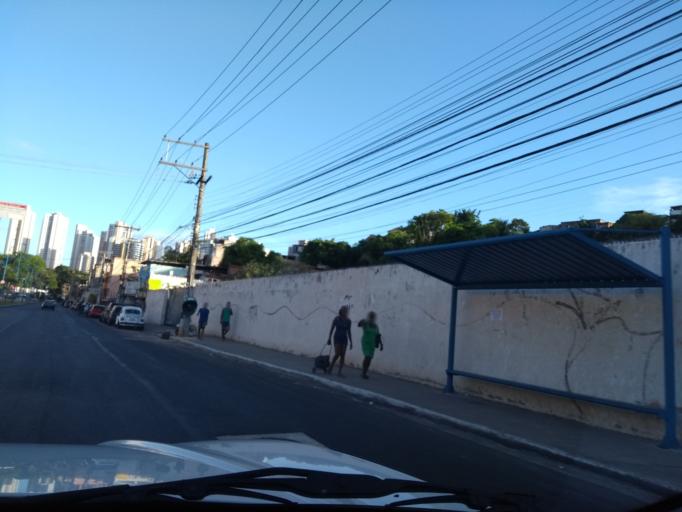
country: BR
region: Bahia
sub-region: Salvador
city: Salvador
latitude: -12.9962
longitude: -38.4955
